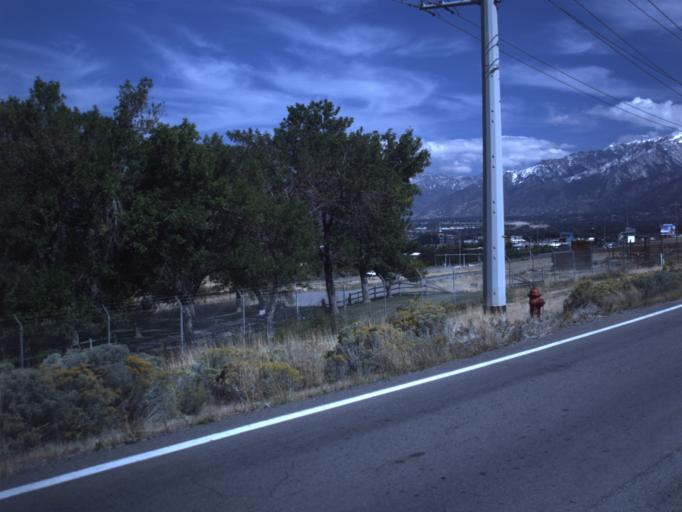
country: US
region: Utah
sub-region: Salt Lake County
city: Bluffdale
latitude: 40.4863
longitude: -111.8985
